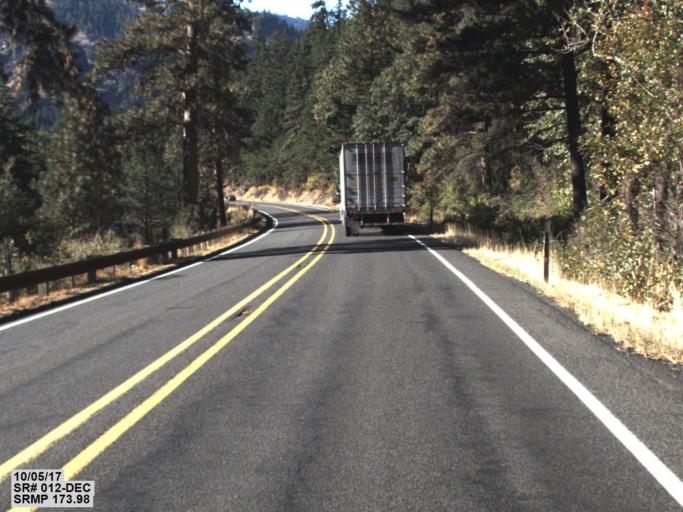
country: US
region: Washington
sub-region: Yakima County
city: Tieton
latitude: 46.6761
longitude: -120.9682
